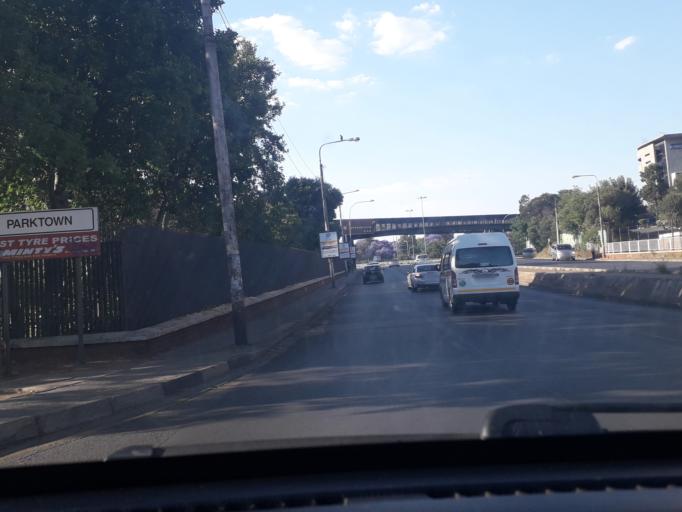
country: ZA
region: Gauteng
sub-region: City of Johannesburg Metropolitan Municipality
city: Johannesburg
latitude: -26.1863
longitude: 28.0323
